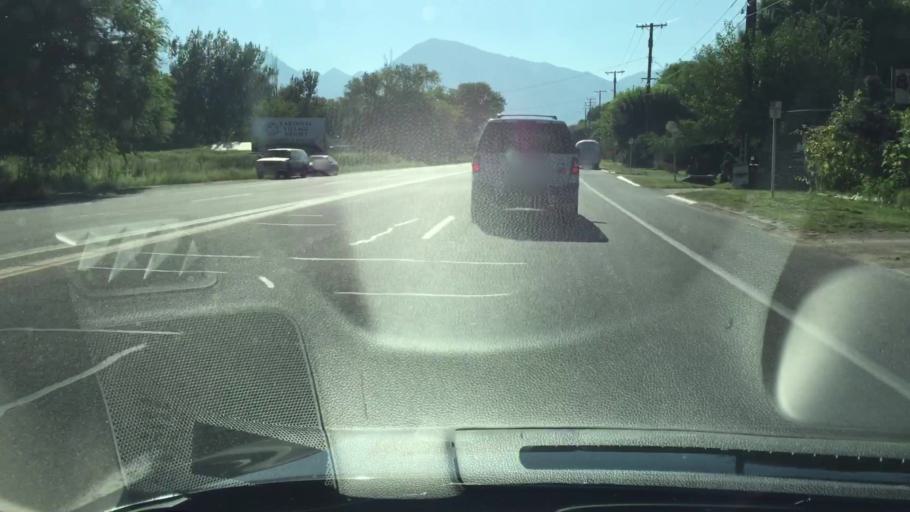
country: US
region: California
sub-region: Inyo County
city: Dixon Lane-Meadow Creek
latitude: 37.3614
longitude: -118.4242
